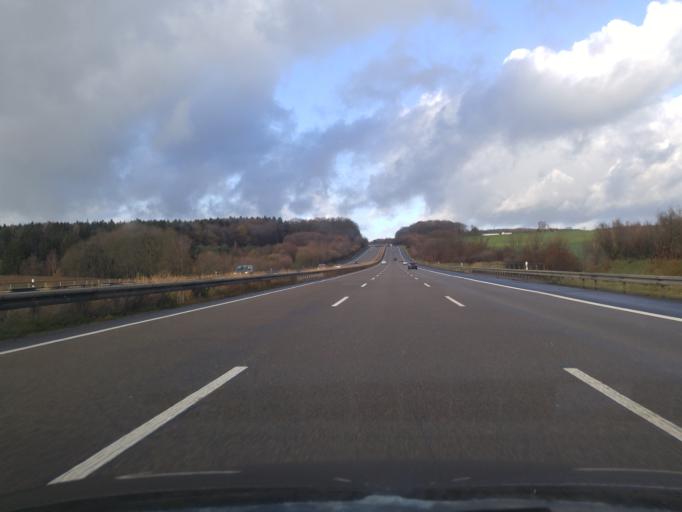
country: DE
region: Hesse
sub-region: Regierungsbezirk Kassel
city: Malsfeld
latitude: 51.0523
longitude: 9.4966
